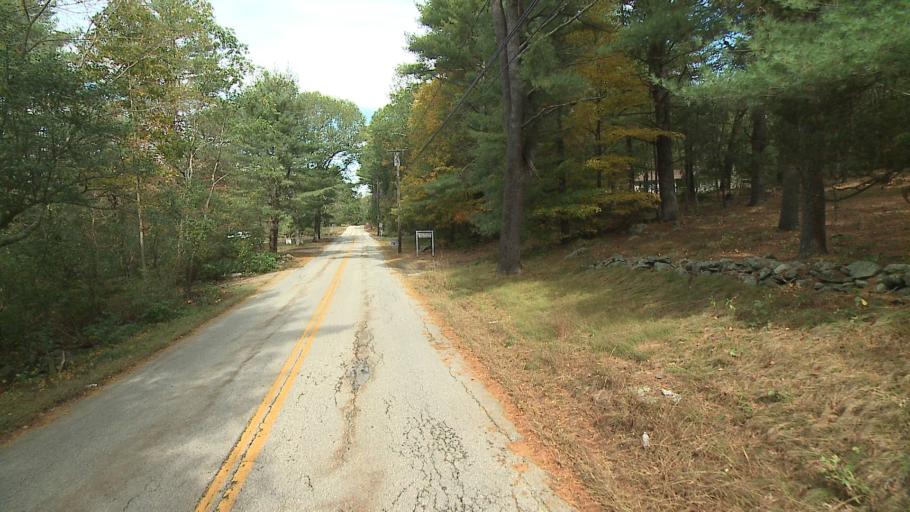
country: US
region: Connecticut
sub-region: Windham County
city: Thompson
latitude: 41.9247
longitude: -71.8217
